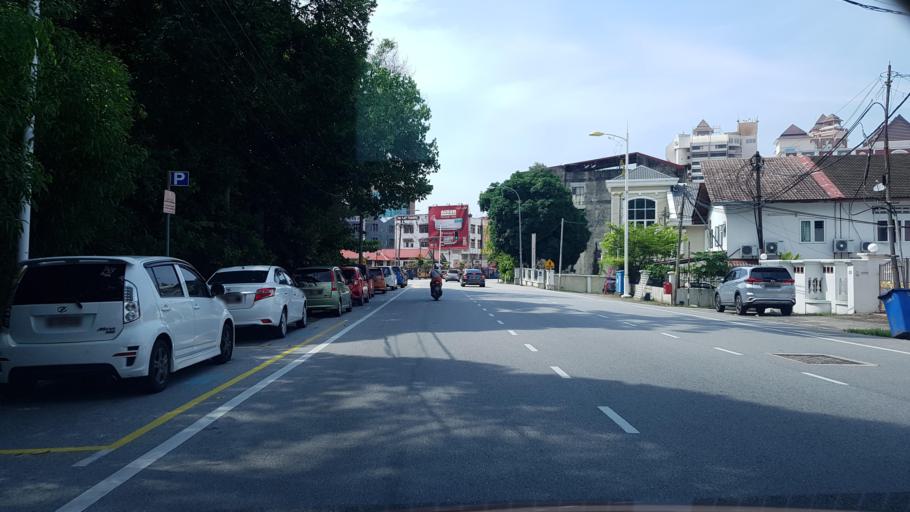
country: MY
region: Terengganu
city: Kuala Terengganu
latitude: 5.3270
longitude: 103.1352
